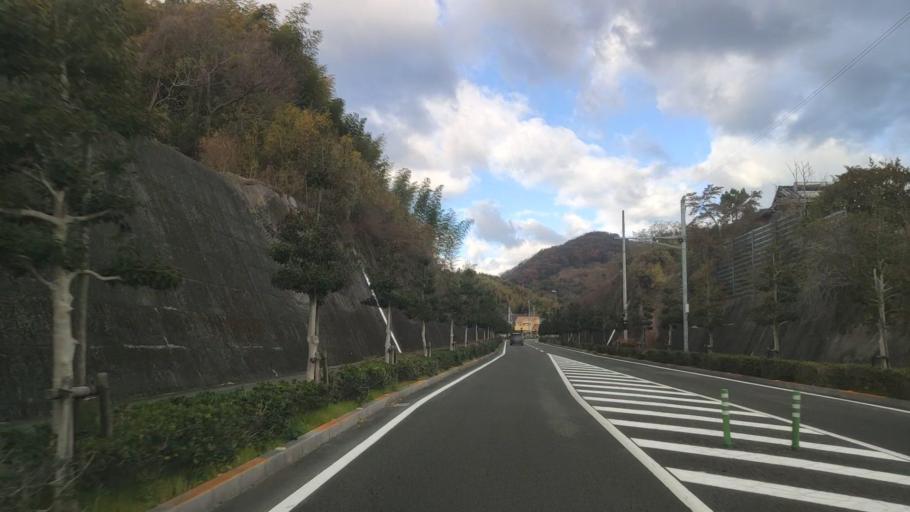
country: JP
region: Ehime
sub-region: Shikoku-chuo Shi
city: Matsuyama
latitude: 33.8736
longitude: 132.7171
